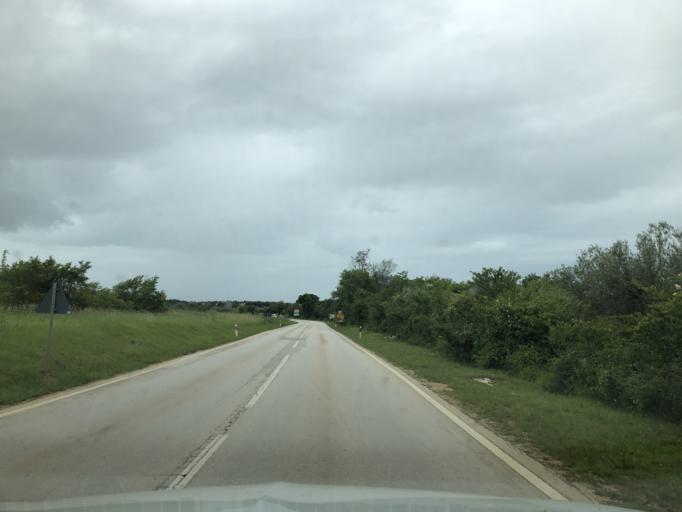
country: HR
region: Istarska
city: Umag
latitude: 45.4496
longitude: 13.5712
